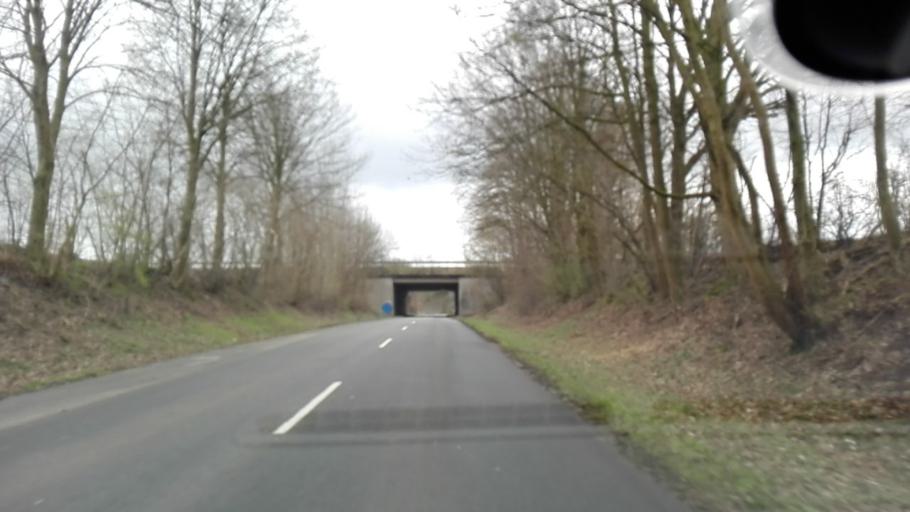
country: DE
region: North Rhine-Westphalia
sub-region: Regierungsbezirk Arnsberg
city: Holzwickede
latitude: 51.5235
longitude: 7.6522
